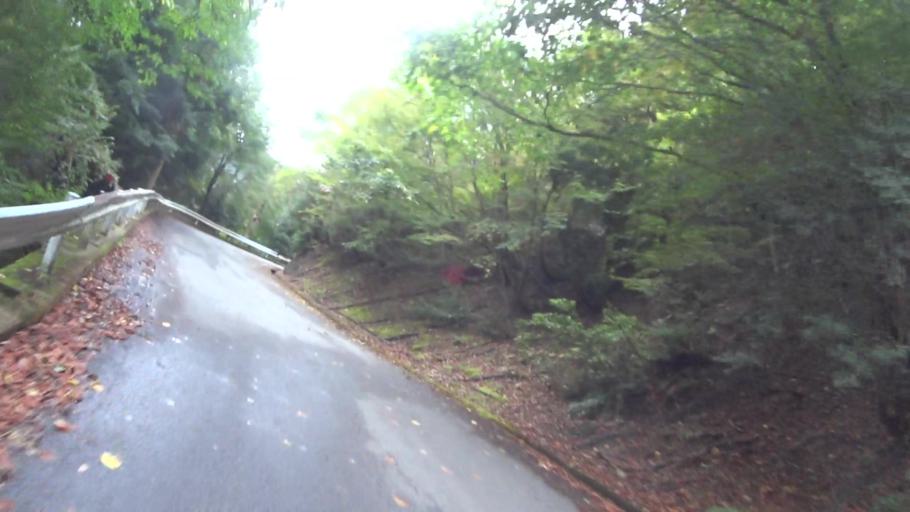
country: JP
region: Shiga Prefecture
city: Kitahama
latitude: 35.2719
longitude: 135.7370
